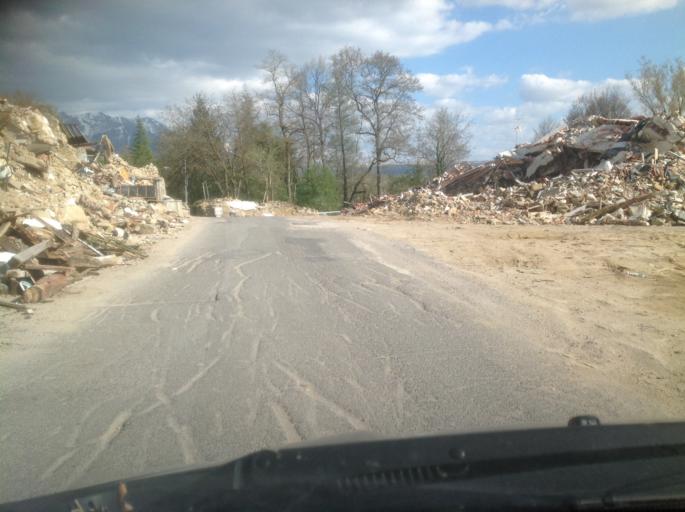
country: IT
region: Latium
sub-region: Provincia di Rieti
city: Amatrice
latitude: 42.6644
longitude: 13.2895
